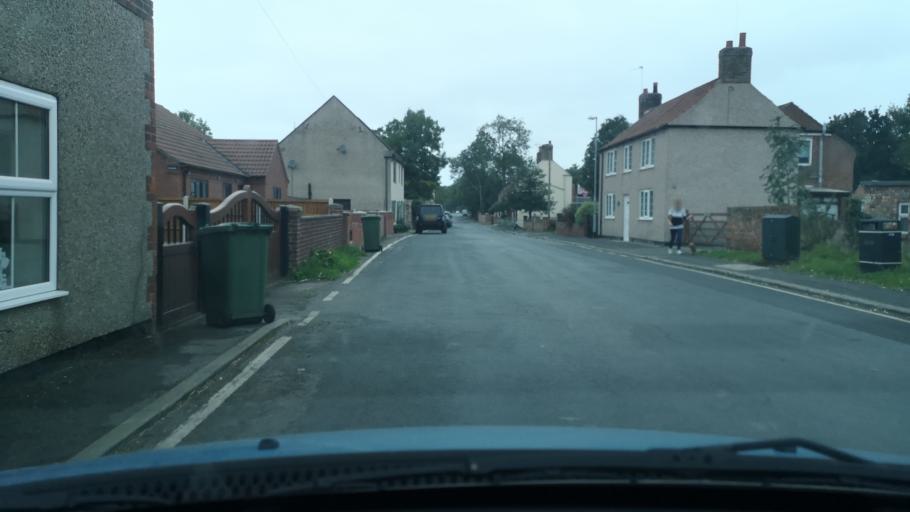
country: GB
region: England
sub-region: East Riding of Yorkshire
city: Laxton
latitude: 53.6983
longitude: -0.7942
